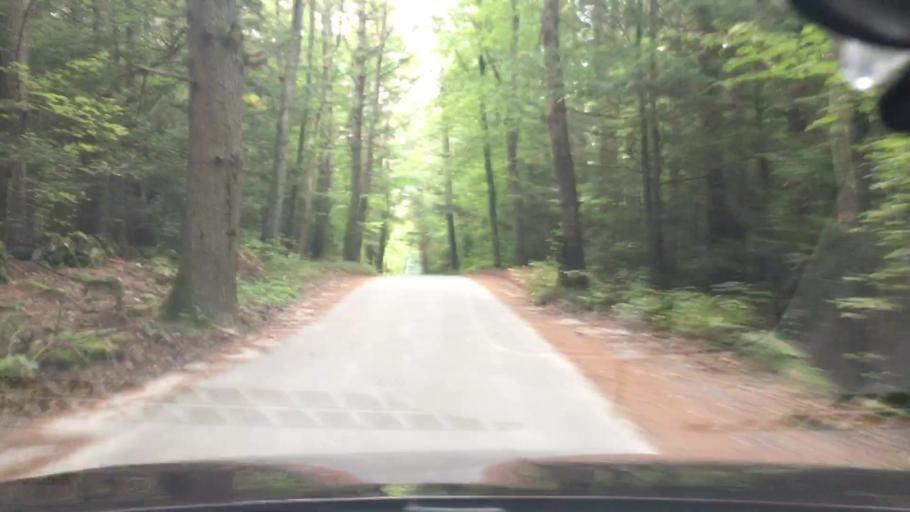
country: US
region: Connecticut
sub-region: Tolland County
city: Stafford
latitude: 41.9859
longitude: -72.3300
